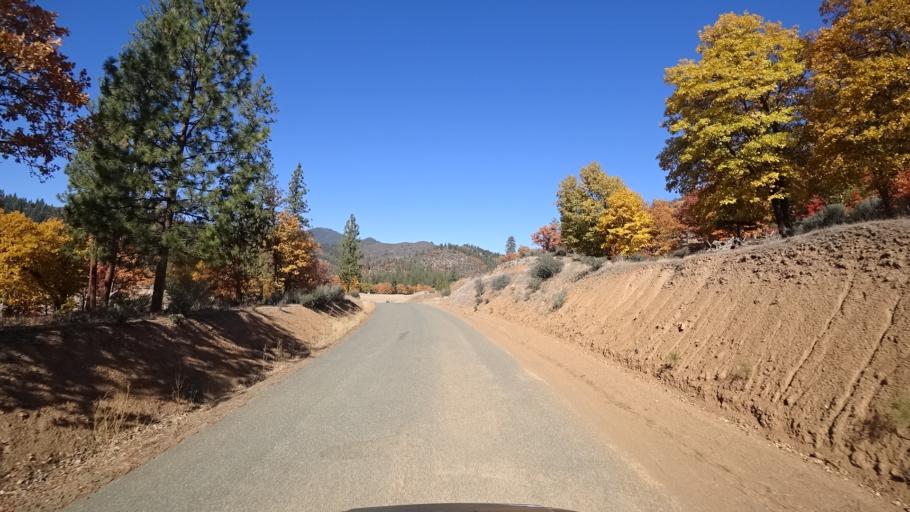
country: US
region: California
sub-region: Siskiyou County
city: Yreka
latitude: 41.6402
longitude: -122.8882
